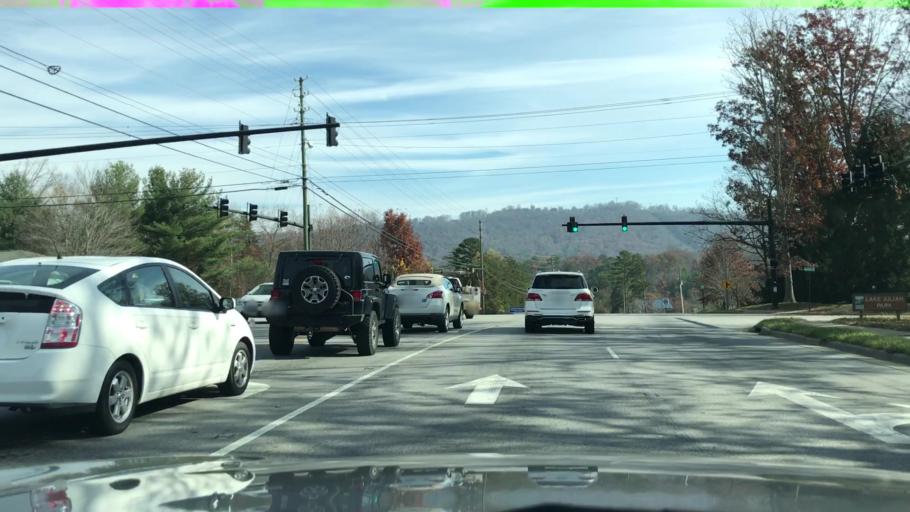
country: US
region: North Carolina
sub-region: Buncombe County
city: Royal Pines
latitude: 35.4831
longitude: -82.5390
